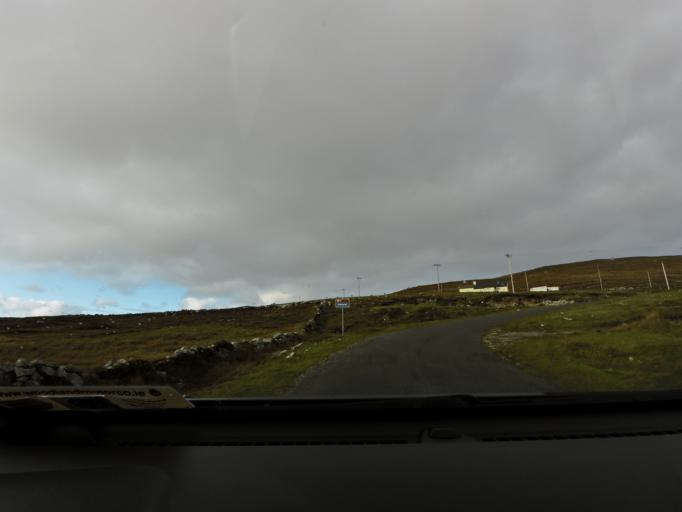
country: IE
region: Connaught
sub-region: Maigh Eo
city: Belmullet
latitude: 53.9057
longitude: -9.9948
